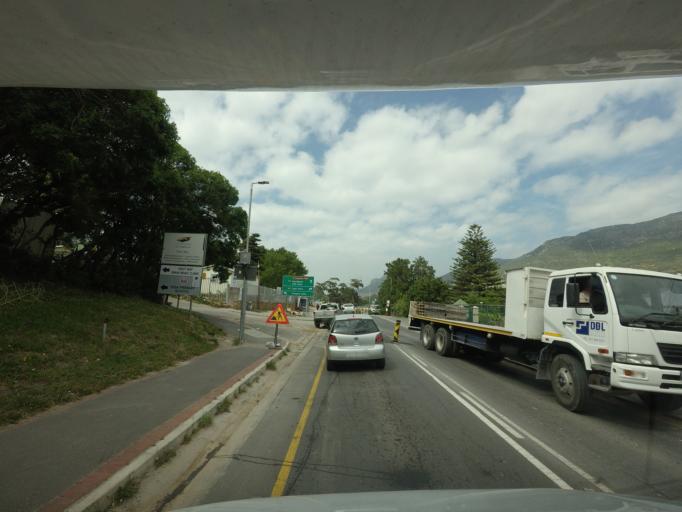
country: ZA
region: Western Cape
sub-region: City of Cape Town
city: Constantia
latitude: -34.0287
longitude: 18.3570
